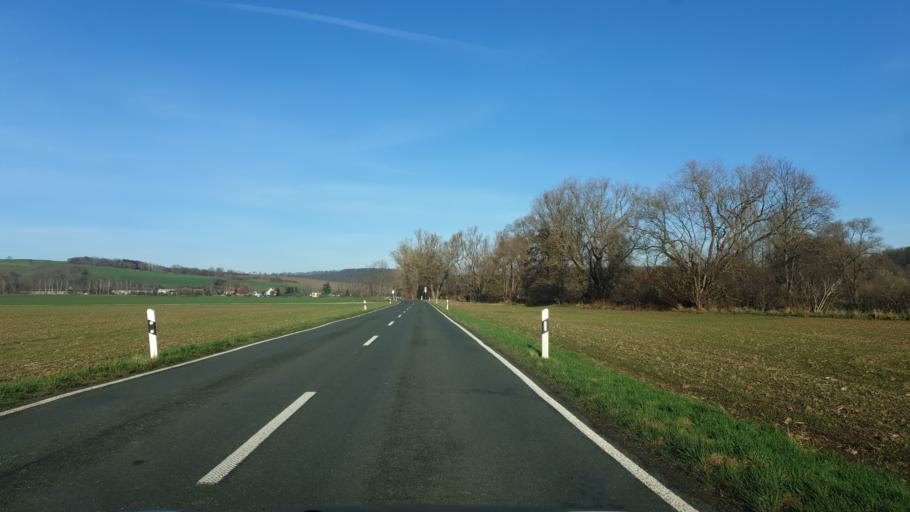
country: DE
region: Saxony-Anhalt
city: Wetterzeube
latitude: 50.9904
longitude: 11.9889
